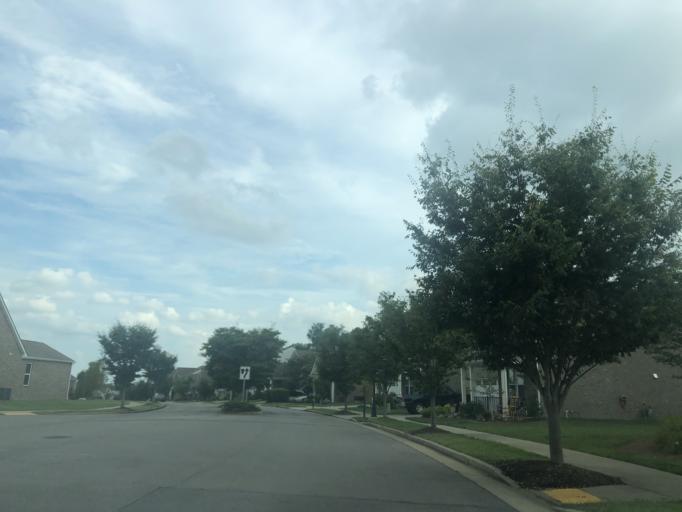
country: US
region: Tennessee
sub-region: Davidson County
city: Lakewood
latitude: 36.1687
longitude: -86.6208
